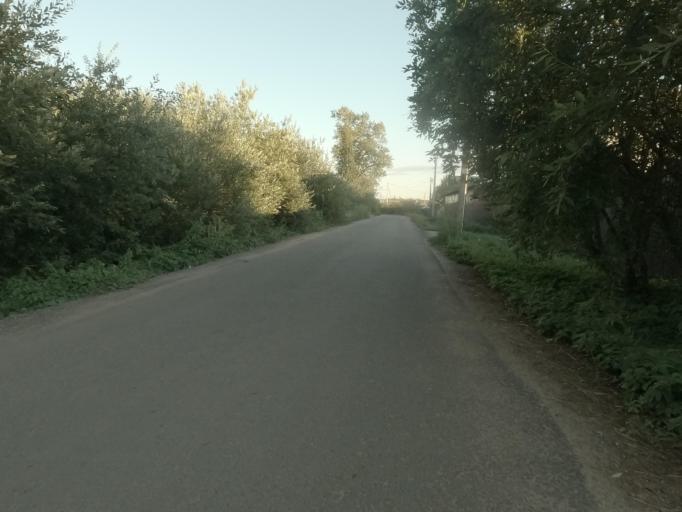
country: RU
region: Leningrad
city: Kirovsk
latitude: 59.8695
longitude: 31.0014
